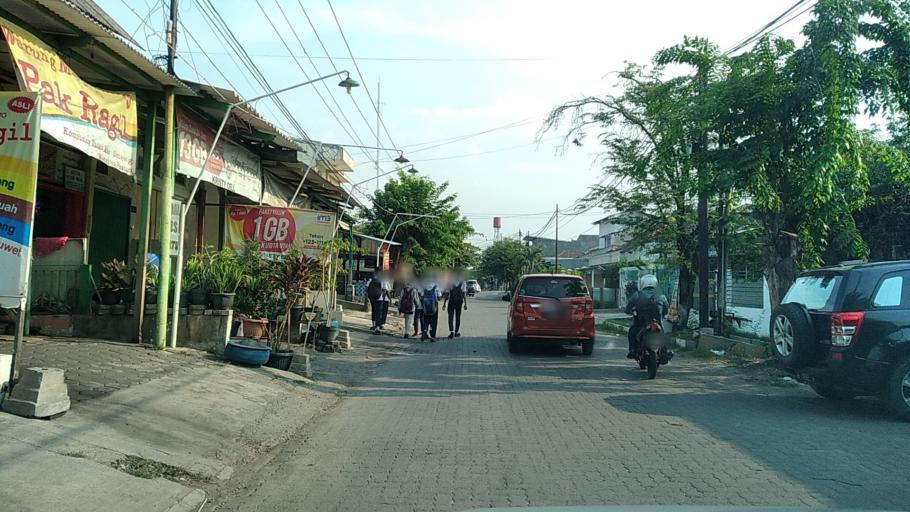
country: ID
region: Central Java
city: Semarang
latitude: -6.9588
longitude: 110.4047
